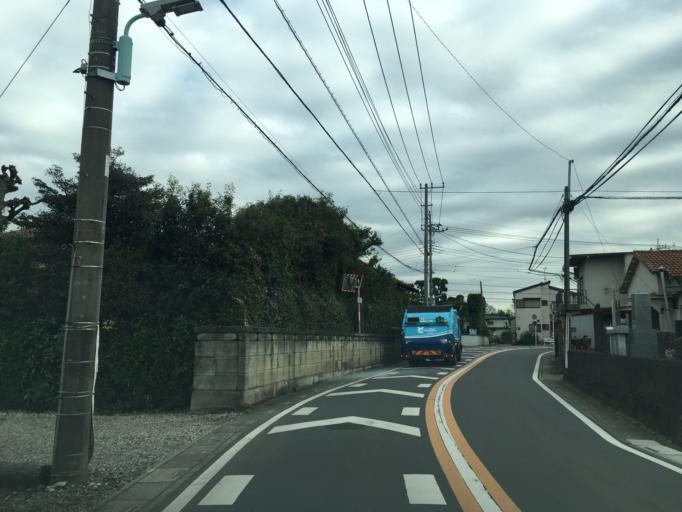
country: JP
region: Saitama
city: Sayama
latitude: 35.7929
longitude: 139.4007
